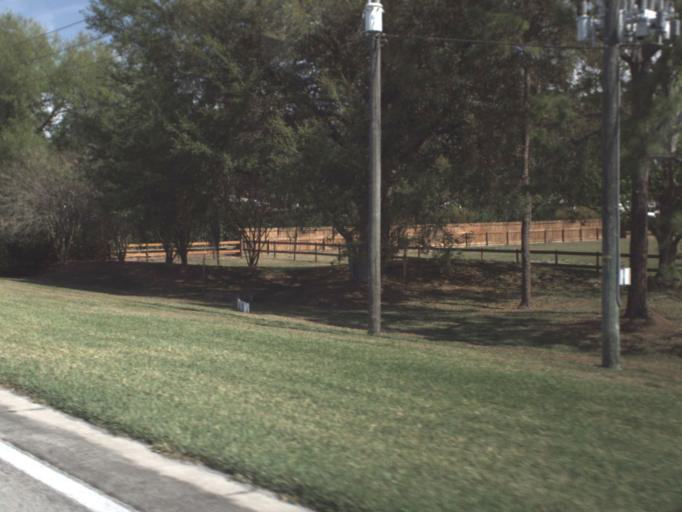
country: US
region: Florida
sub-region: Sumter County
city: The Villages
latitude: 28.9444
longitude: -81.9492
